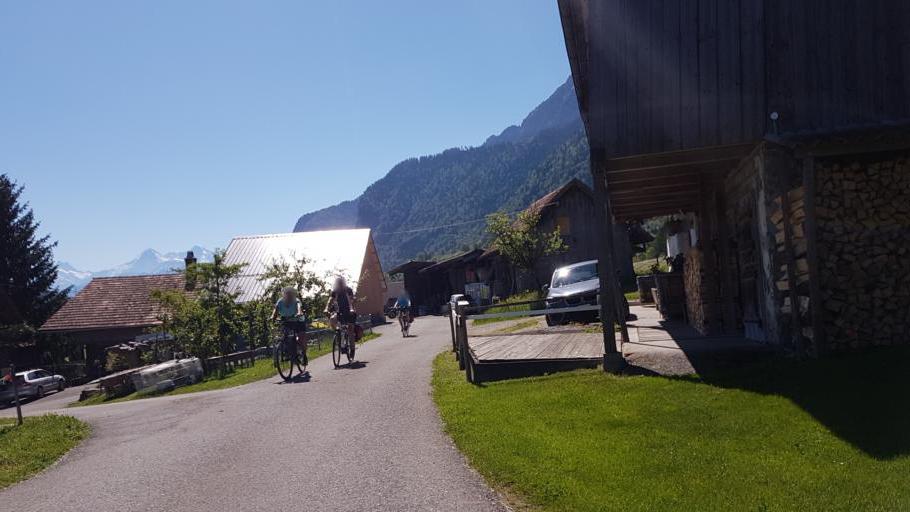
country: CH
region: Bern
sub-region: Thun District
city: Blumenstein
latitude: 46.7228
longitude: 7.5396
